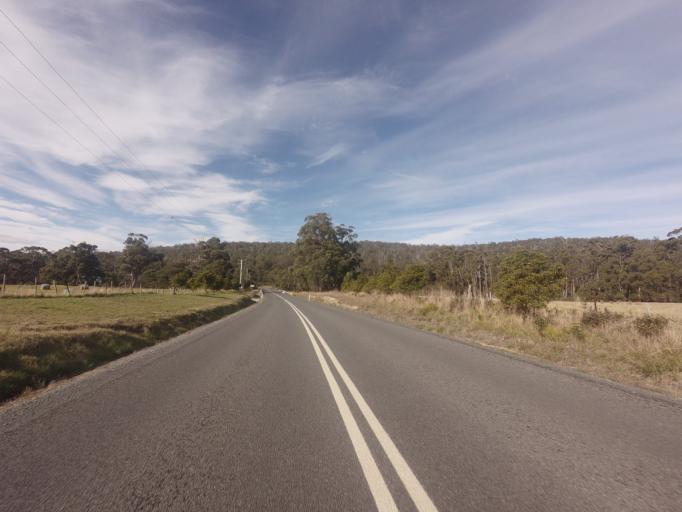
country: AU
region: Tasmania
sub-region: Clarence
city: Sandford
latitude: -43.0643
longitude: 147.8378
